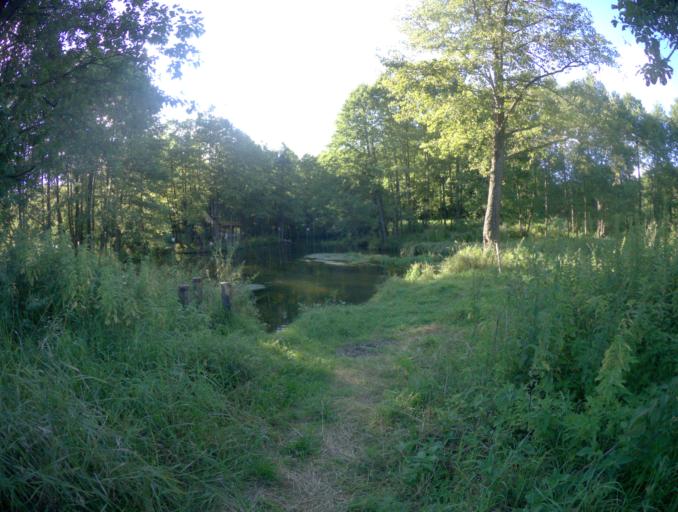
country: RU
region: Vladimir
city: Krasnaya Gorbatka
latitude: 55.7877
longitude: 41.6557
